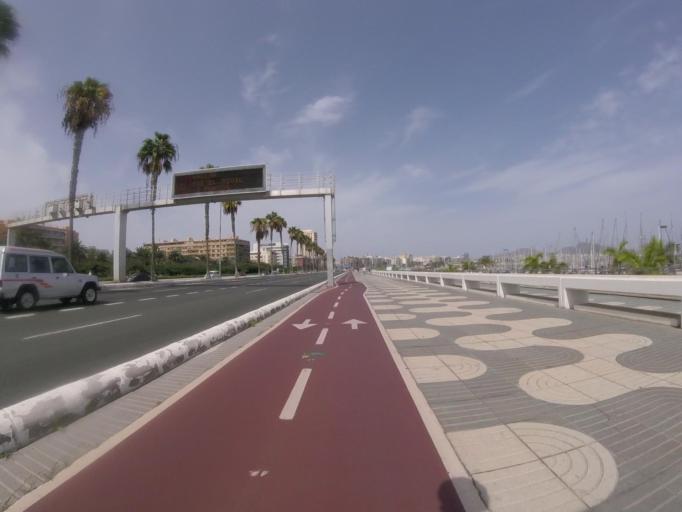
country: ES
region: Canary Islands
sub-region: Provincia de Las Palmas
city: Las Palmas de Gran Canaria
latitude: 28.1251
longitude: -15.4269
